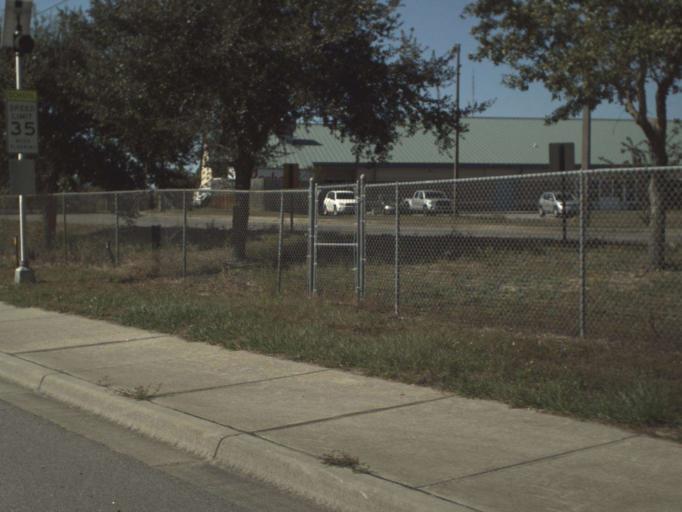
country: US
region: Florida
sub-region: Walton County
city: Seaside
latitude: 30.3788
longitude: -86.1787
